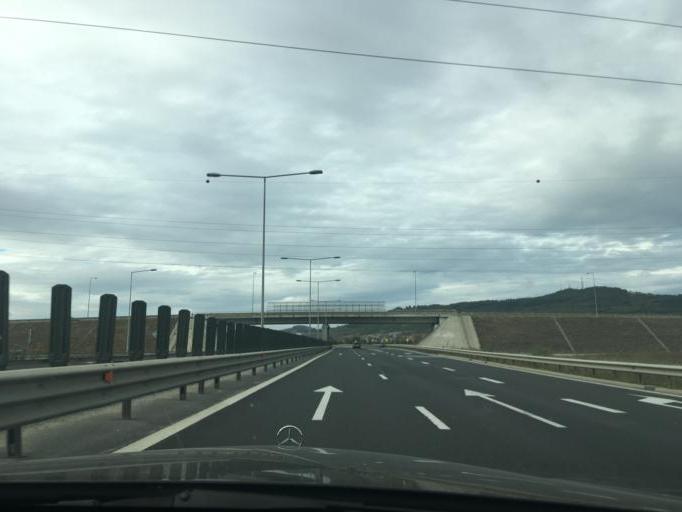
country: RO
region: Sibiu
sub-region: Comuna Selimbar
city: Selimbar
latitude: 45.7876
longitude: 24.1996
